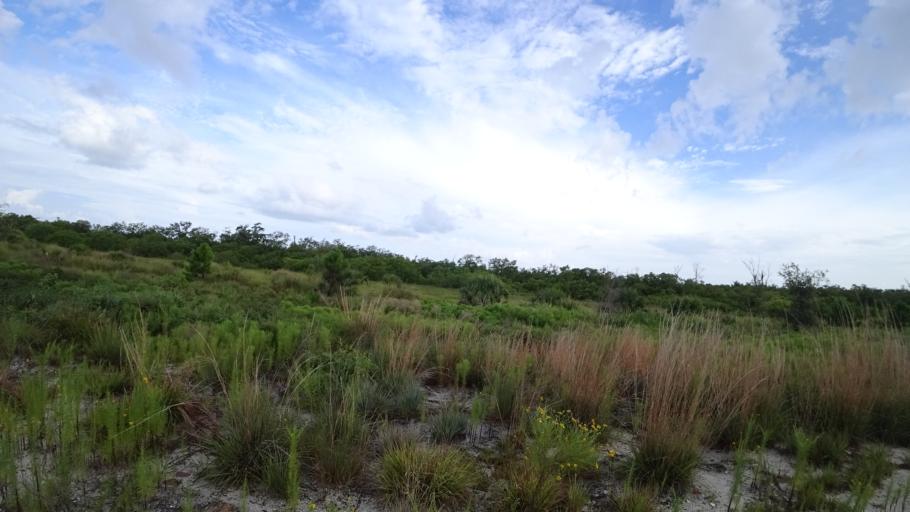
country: US
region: Florida
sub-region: Manatee County
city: Holmes Beach
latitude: 27.5028
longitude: -82.6773
